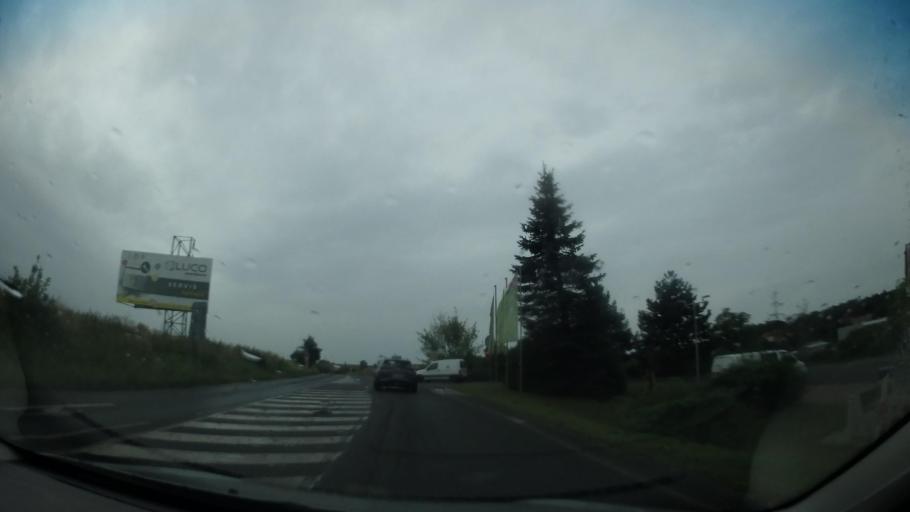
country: CZ
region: Central Bohemia
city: Milovice
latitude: 50.2234
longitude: 14.8779
